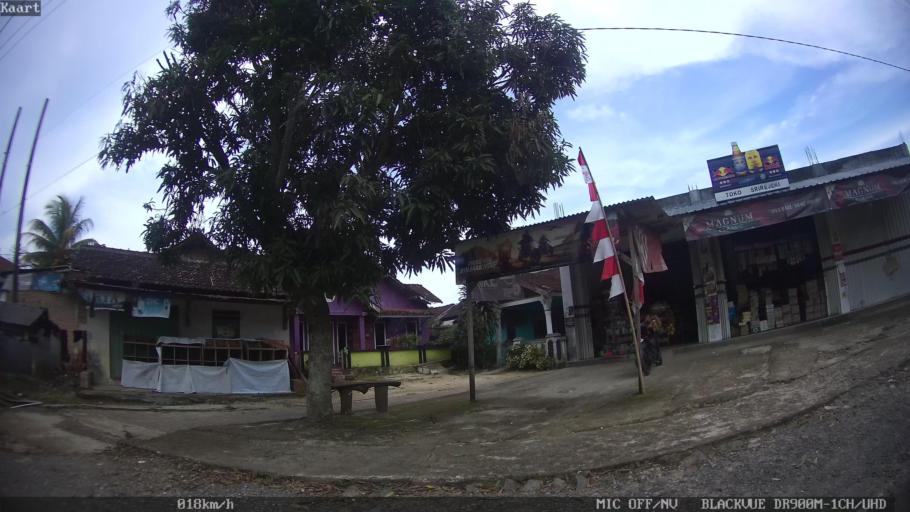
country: ID
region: Lampung
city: Bandarlampung
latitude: -5.4157
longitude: 105.1892
